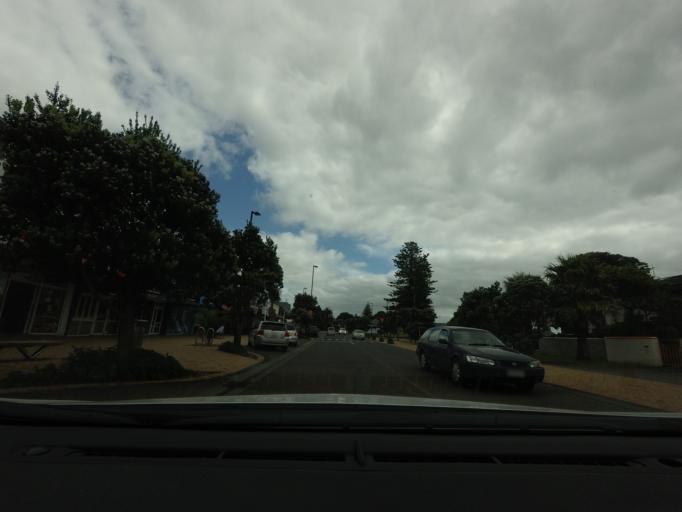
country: NZ
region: Auckland
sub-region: Auckland
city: Rothesay Bay
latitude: -36.5868
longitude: 174.6964
